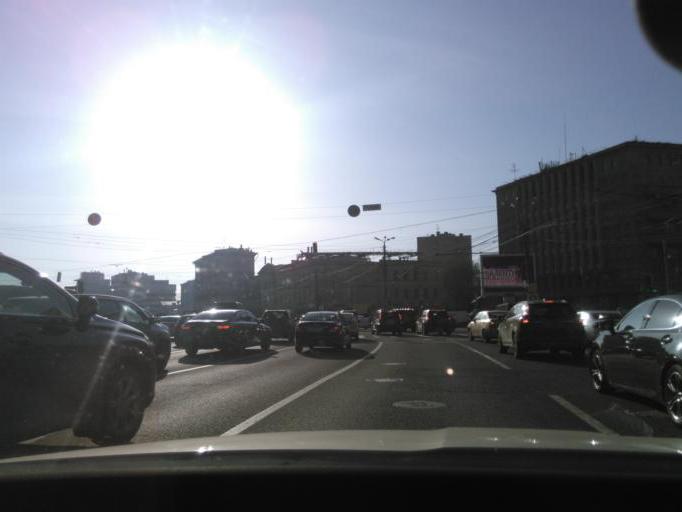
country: RU
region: Moskovskaya
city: Dorogomilovo
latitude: 55.7390
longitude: 37.5855
